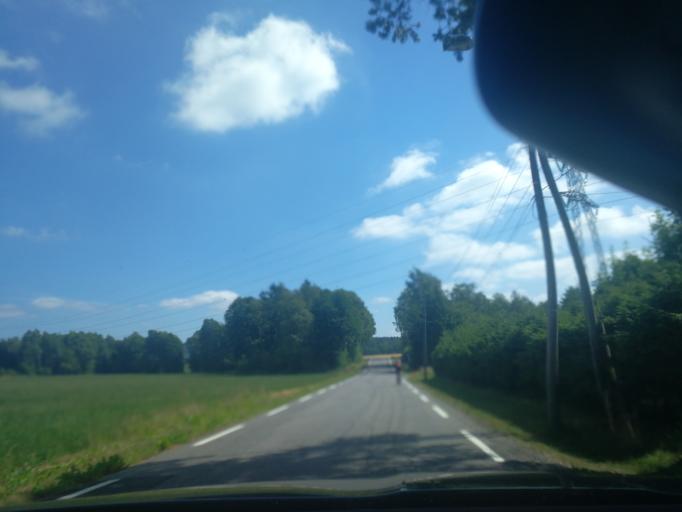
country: NO
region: Vestfold
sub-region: Stokke
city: Stokke
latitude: 59.2061
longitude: 10.2502
